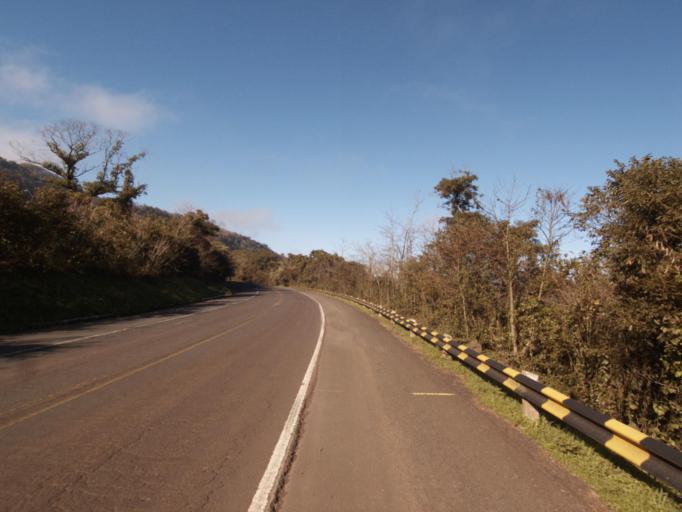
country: BR
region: Rio Grande do Sul
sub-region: Frederico Westphalen
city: Frederico Westphalen
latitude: -26.9880
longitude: -53.2268
